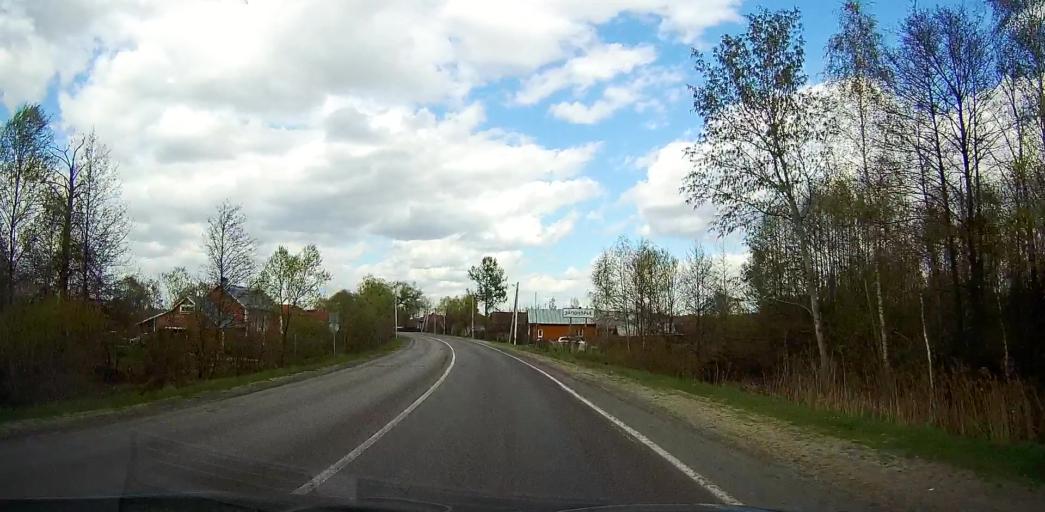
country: RU
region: Moskovskaya
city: Davydovo
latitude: 55.6328
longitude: 38.8685
